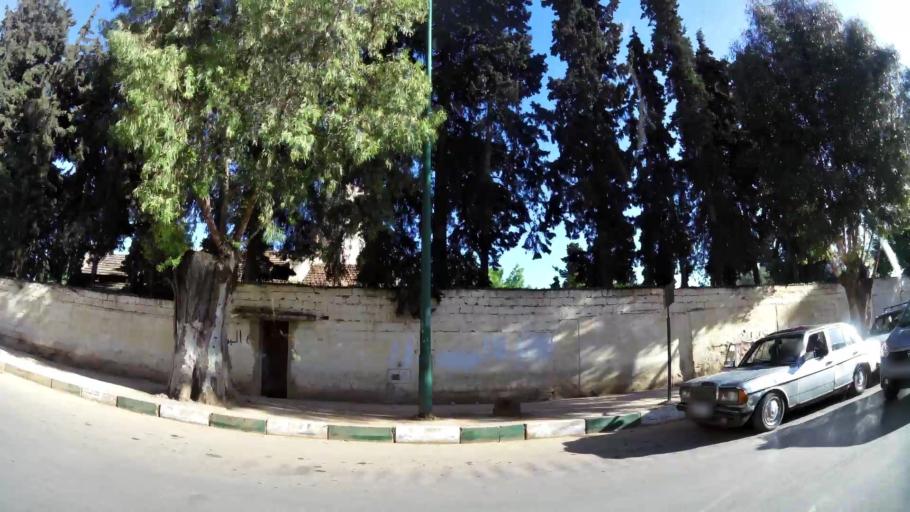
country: MA
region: Meknes-Tafilalet
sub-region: Meknes
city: Meknes
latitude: 33.8921
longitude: -5.5375
